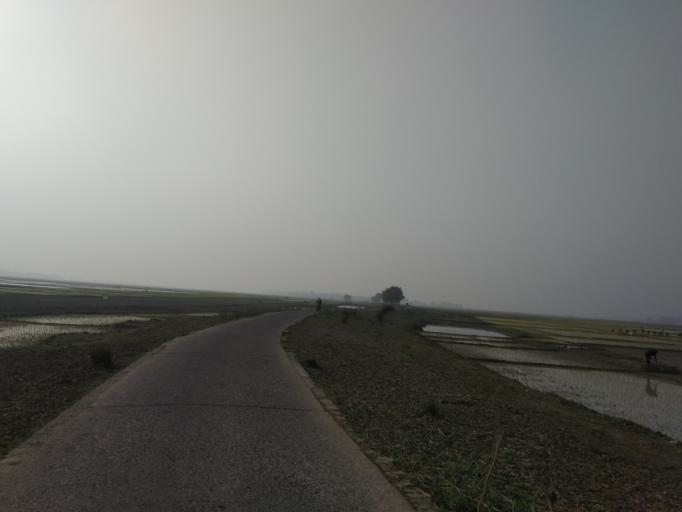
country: BD
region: Rajshahi
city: Ishurdi
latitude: 24.4837
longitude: 89.2199
